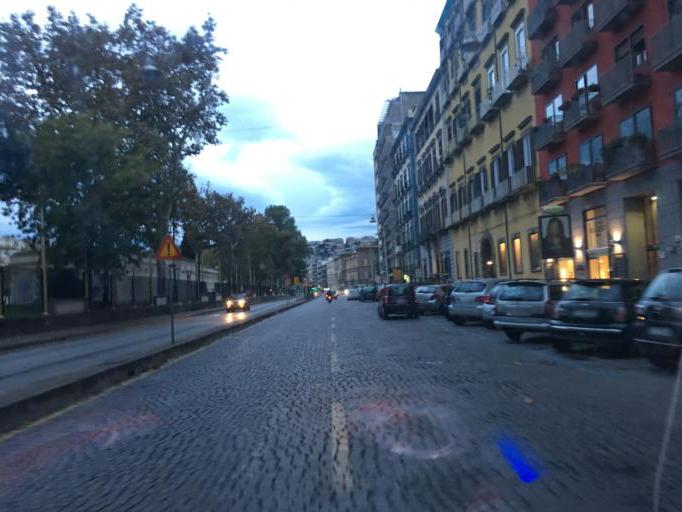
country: IT
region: Campania
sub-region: Provincia di Napoli
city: Napoli
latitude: 40.8333
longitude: 14.2377
